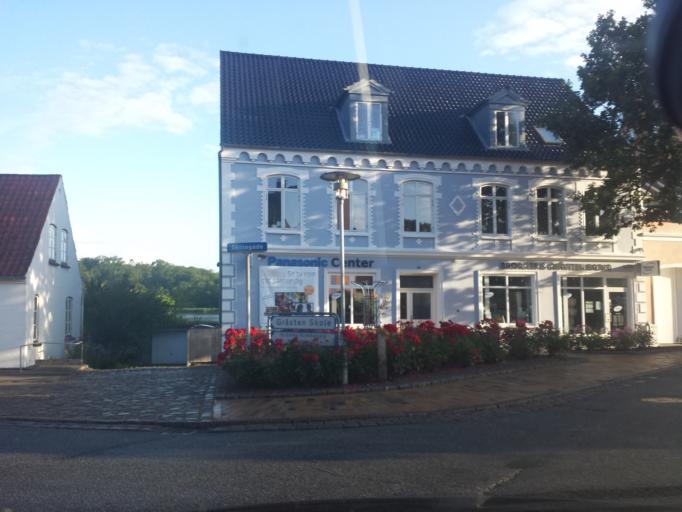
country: DK
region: South Denmark
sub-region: Sonderborg Kommune
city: Grasten
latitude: 54.9208
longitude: 9.5910
